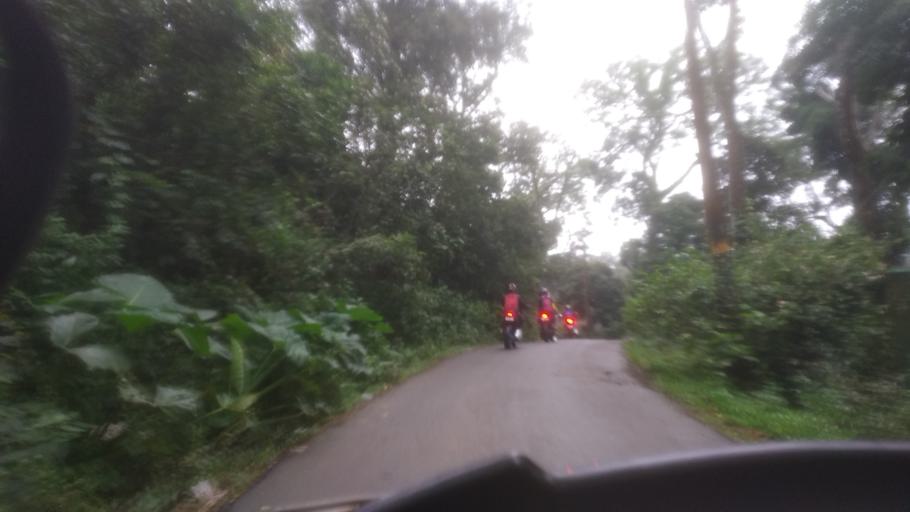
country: IN
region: Tamil Nadu
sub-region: Theni
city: Kombai
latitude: 9.8941
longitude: 77.2120
